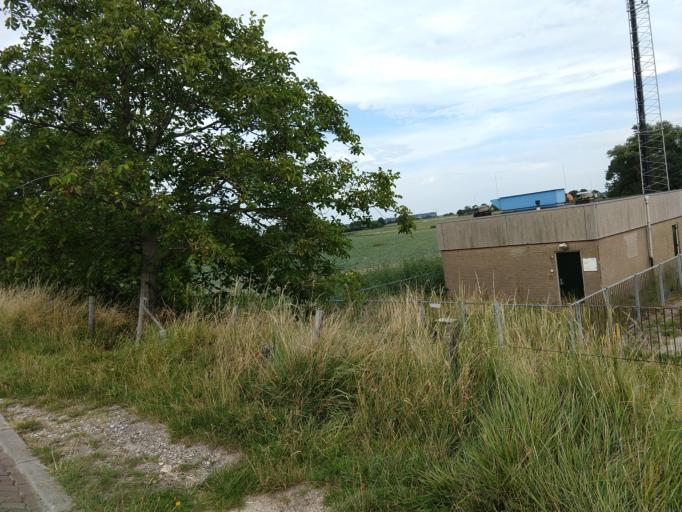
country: NL
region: Zeeland
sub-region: Gemeente Borsele
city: Borssele
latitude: 51.4724
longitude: 3.7405
